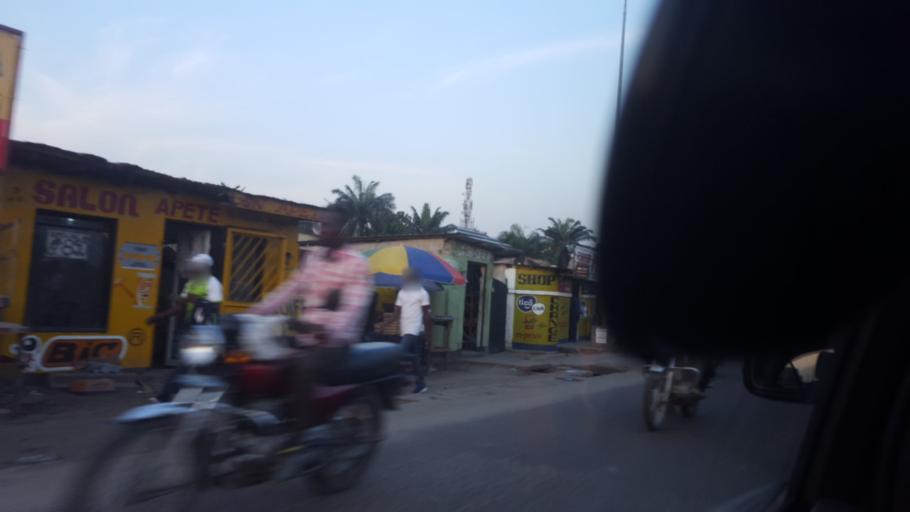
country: CD
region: Kinshasa
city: Kinshasa
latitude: -4.3521
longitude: 15.3274
